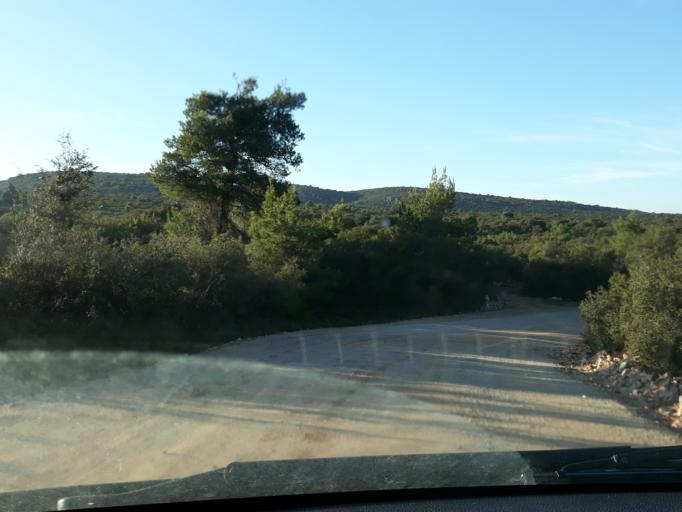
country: GR
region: Central Greece
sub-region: Nomos Voiotias
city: Ayios Thomas
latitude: 38.2364
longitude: 23.5328
